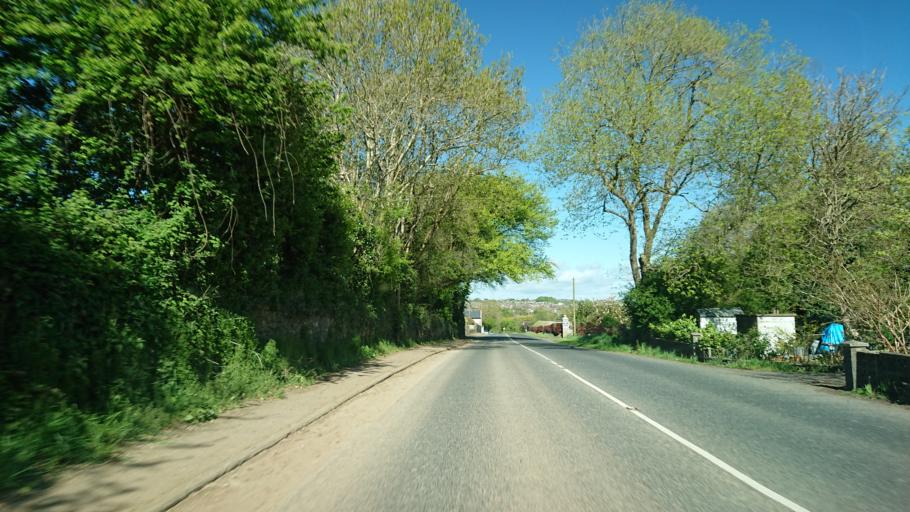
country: IE
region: Munster
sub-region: Waterford
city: Waterford
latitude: 52.2344
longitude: -7.0538
